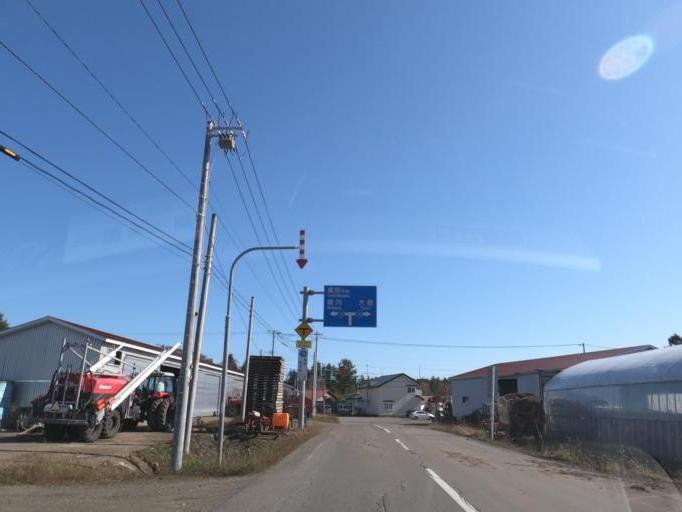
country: JP
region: Hokkaido
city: Obihiro
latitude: 42.6759
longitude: 143.3102
